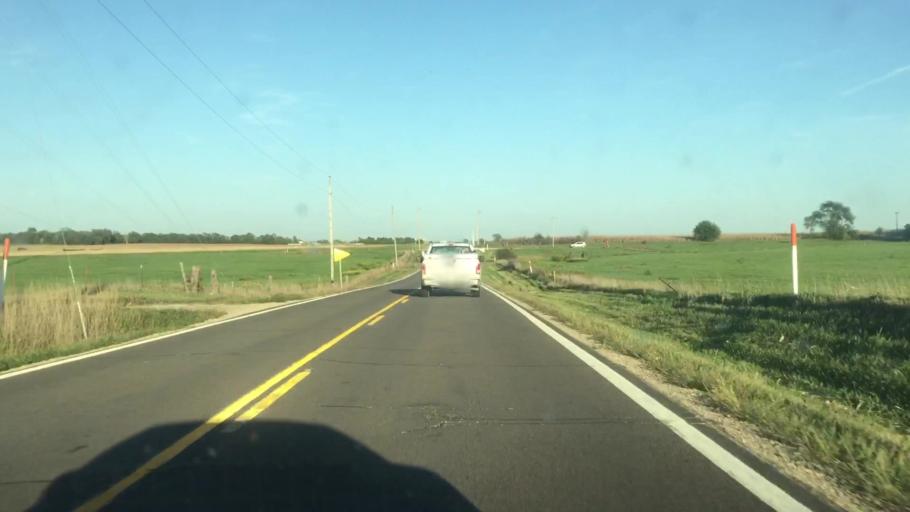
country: US
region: Kansas
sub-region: Brown County
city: Horton
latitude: 39.5513
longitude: -95.4238
